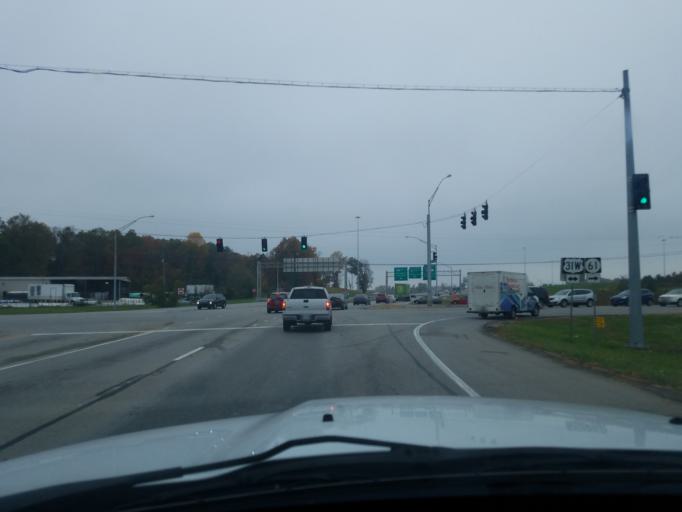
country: US
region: Kentucky
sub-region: Hardin County
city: Elizabethtown
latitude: 37.6698
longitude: -85.8461
